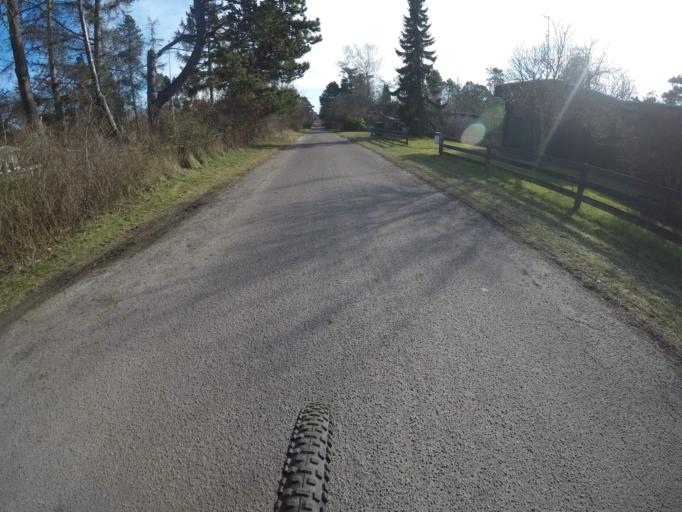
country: DK
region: Capital Region
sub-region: Halsnaes Kommune
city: Liseleje
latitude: 55.9953
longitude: 11.9352
